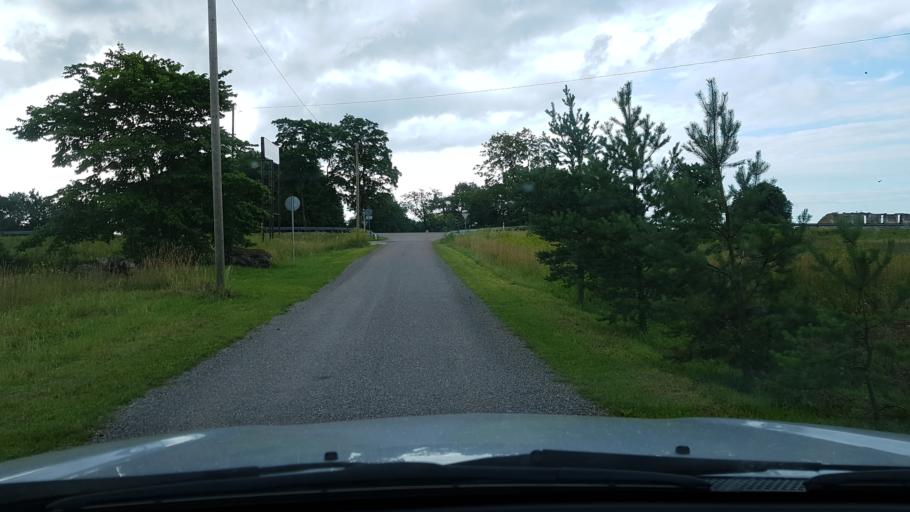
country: EE
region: Ida-Virumaa
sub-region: Narva-Joesuu linn
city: Narva-Joesuu
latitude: 59.3902
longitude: 27.9780
